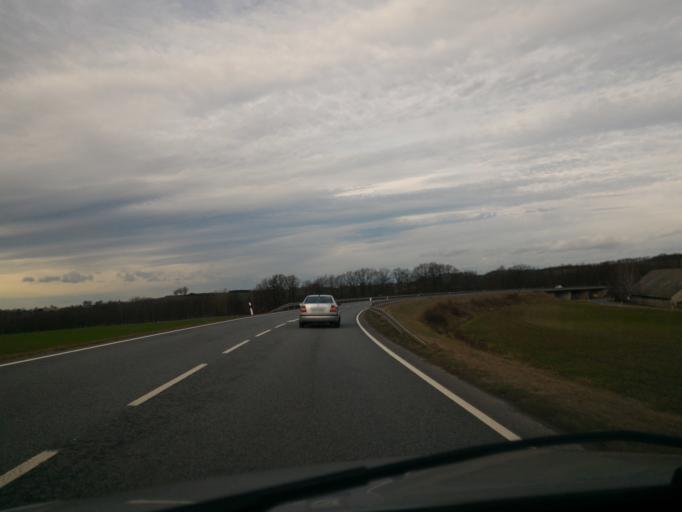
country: DE
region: Saxony
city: Bischofswerda
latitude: 51.1154
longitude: 14.1688
